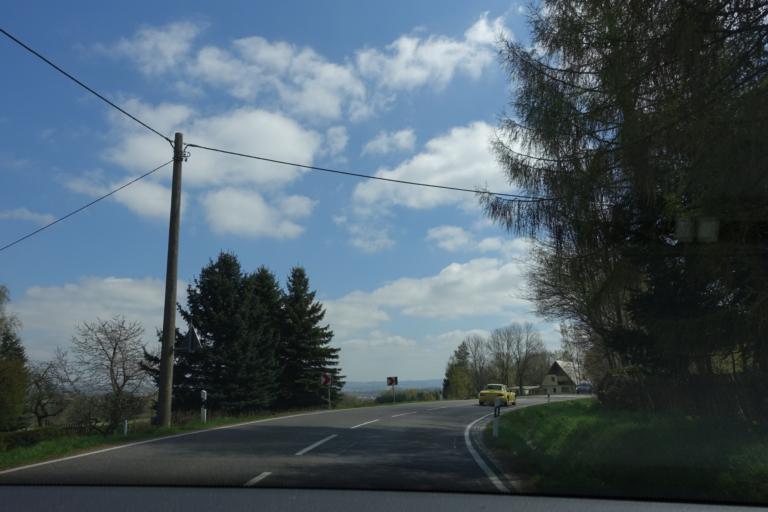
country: DE
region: Saxony
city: Limbach-Oberfrohna
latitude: 50.8408
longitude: 12.8161
